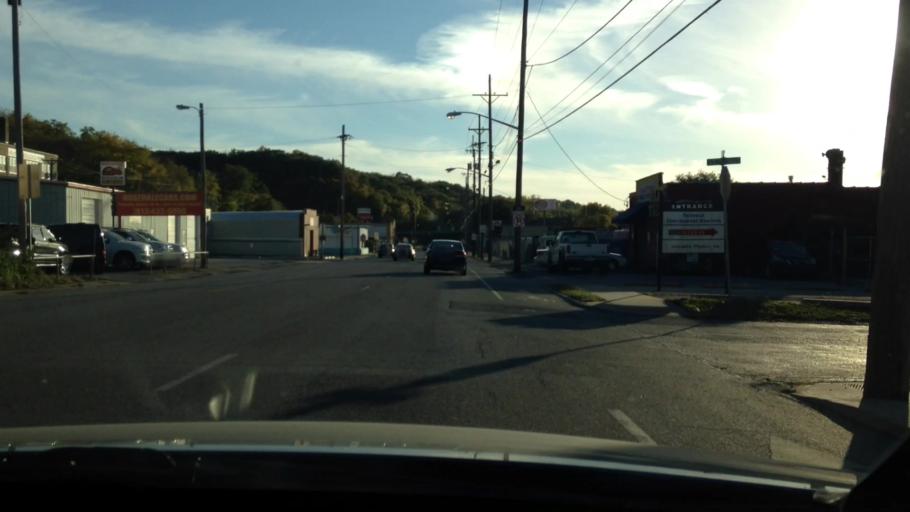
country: US
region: Kansas
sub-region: Johnson County
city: Westwood
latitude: 39.0613
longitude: -94.6210
